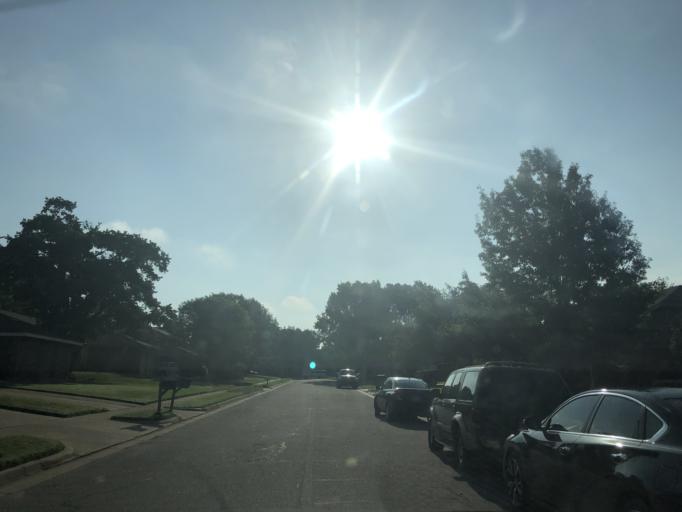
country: US
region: Texas
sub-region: Tarrant County
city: Euless
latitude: 32.8718
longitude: -97.0801
